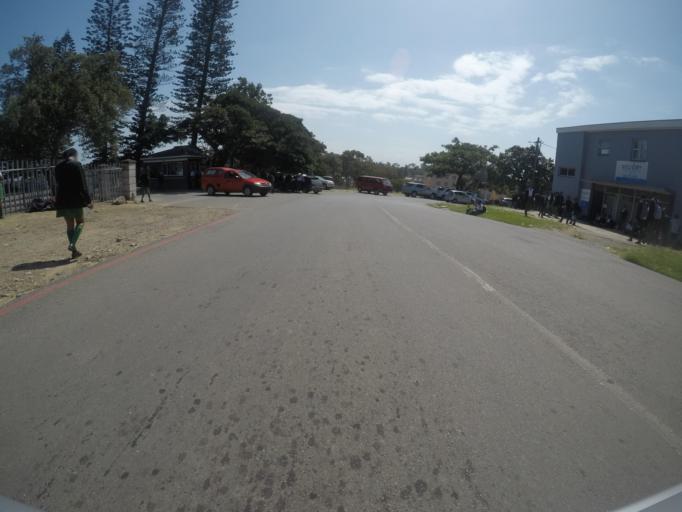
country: ZA
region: Eastern Cape
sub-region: Buffalo City Metropolitan Municipality
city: East London
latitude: -32.9811
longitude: 27.8833
